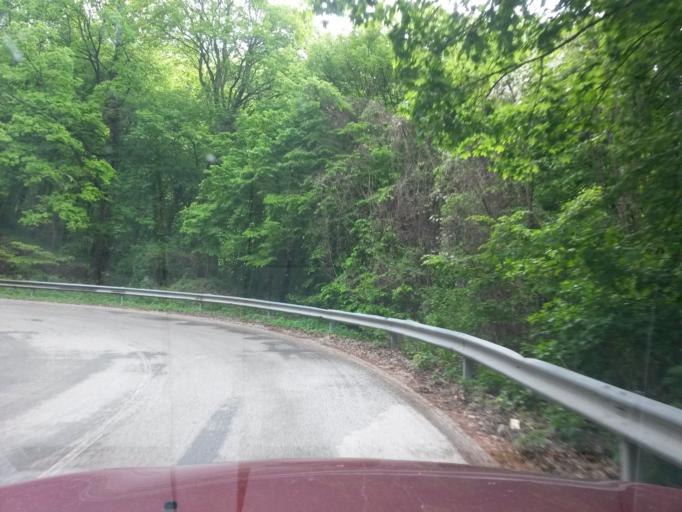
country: SK
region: Kosicky
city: Roznava
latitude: 48.5619
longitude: 20.4731
